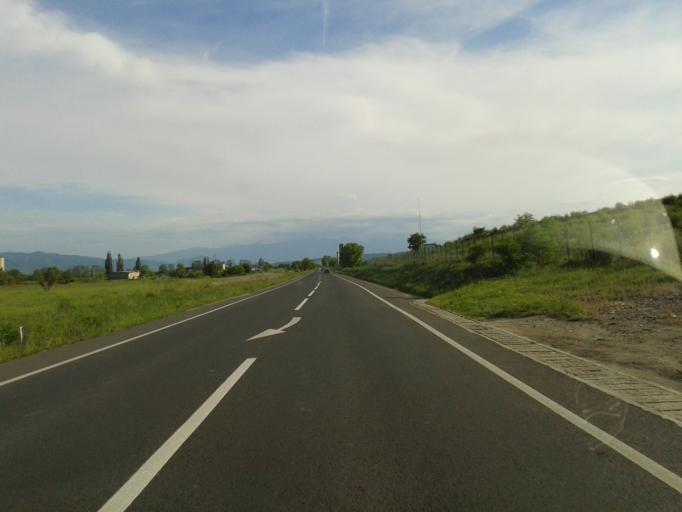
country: RO
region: Hunedoara
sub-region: Comuna Calan
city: Calan
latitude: 45.7484
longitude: 23.0006
